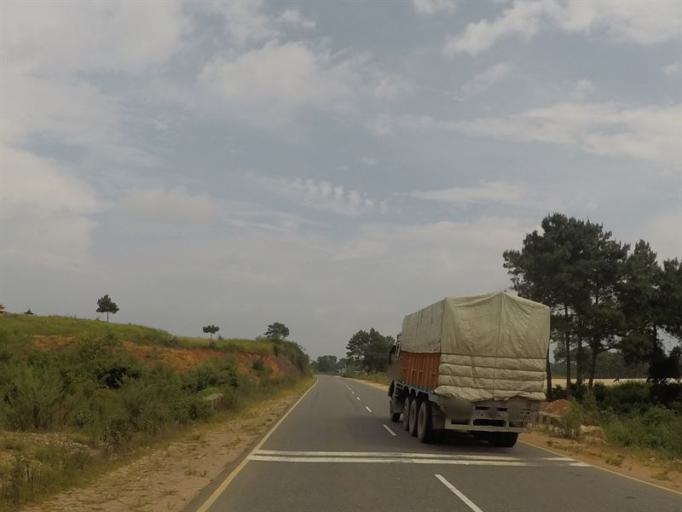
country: IN
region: Meghalaya
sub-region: East Khasi Hills
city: Shillong
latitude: 25.4908
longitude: 92.1853
